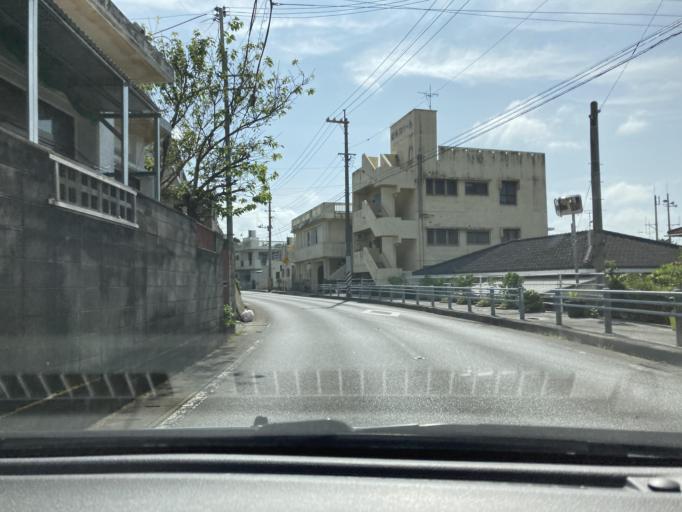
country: JP
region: Okinawa
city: Chatan
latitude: 26.2918
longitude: 127.7985
